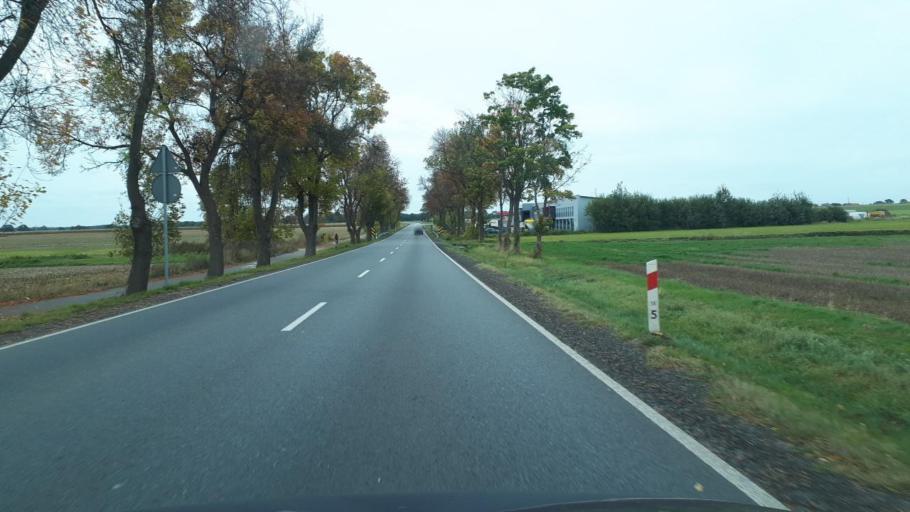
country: PL
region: Opole Voivodeship
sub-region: Powiat oleski
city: Dobrodzien
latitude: 50.7404
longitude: 18.4431
